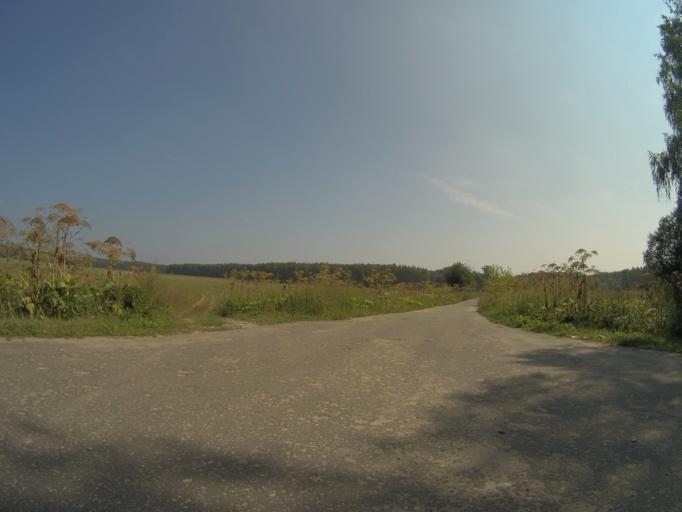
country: RU
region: Vladimir
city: Anopino
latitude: 55.7350
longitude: 40.7221
